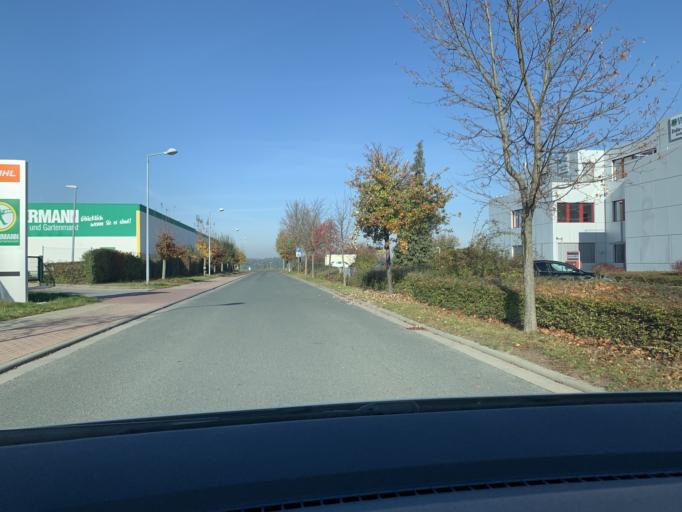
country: DE
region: Thuringia
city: Schmolln
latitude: 50.8837
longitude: 12.3490
